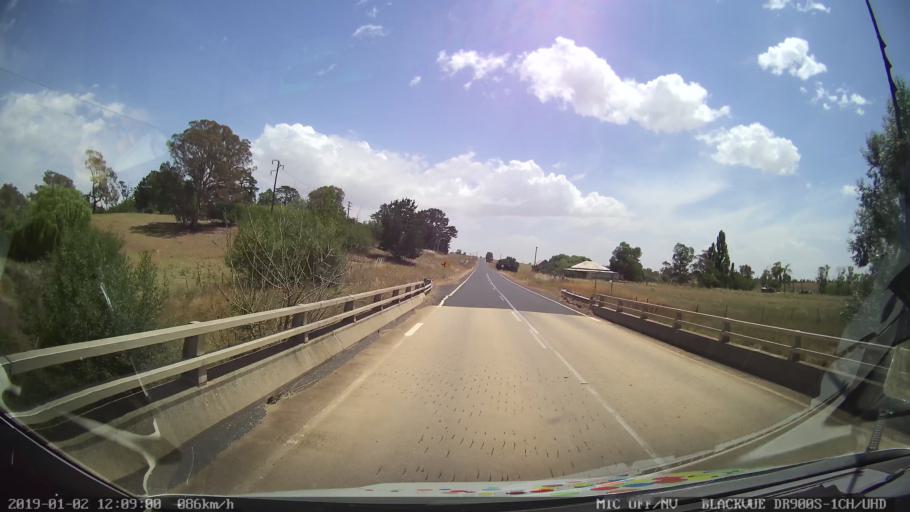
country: AU
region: New South Wales
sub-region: Young
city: Young
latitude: -34.4775
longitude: 148.2722
